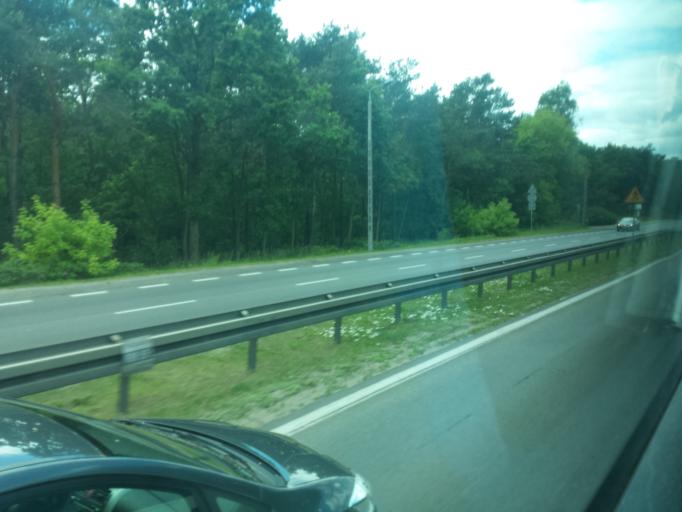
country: PL
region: Masovian Voivodeship
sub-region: Warszawa
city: Wesola
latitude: 52.2243
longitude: 21.2083
